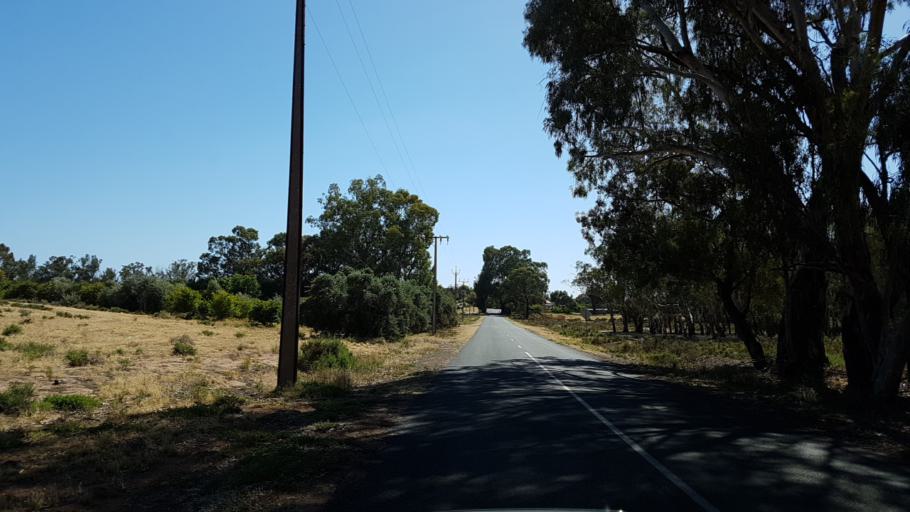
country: AU
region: South Australia
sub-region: Loxton Waikerie
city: Waikerie
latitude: -34.1672
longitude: 140.0264
